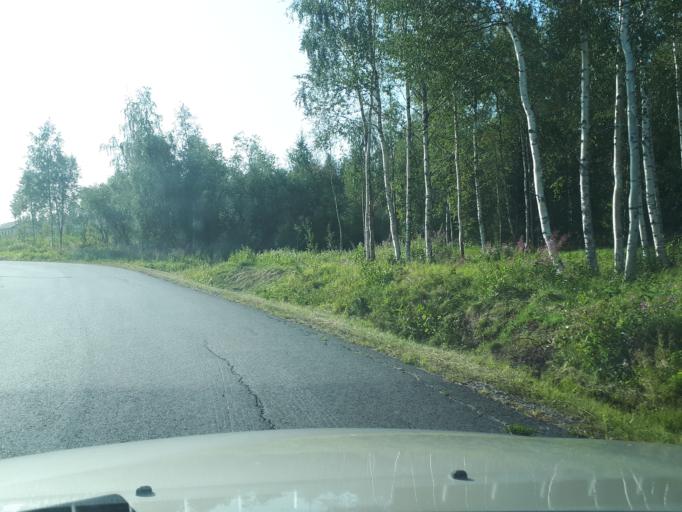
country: FI
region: Northern Ostrobothnia
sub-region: Oulunkaari
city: Ii
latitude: 65.3063
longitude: 25.3677
